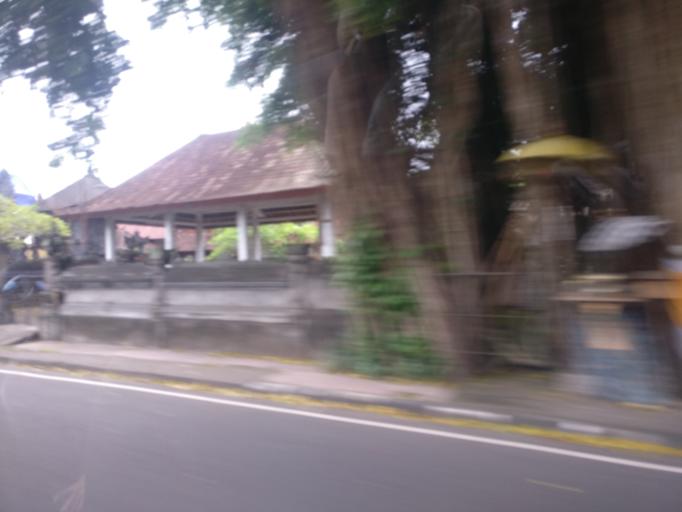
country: ID
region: Bali
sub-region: Kabupaten Gianyar
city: Ubud
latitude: -8.5571
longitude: 115.3021
